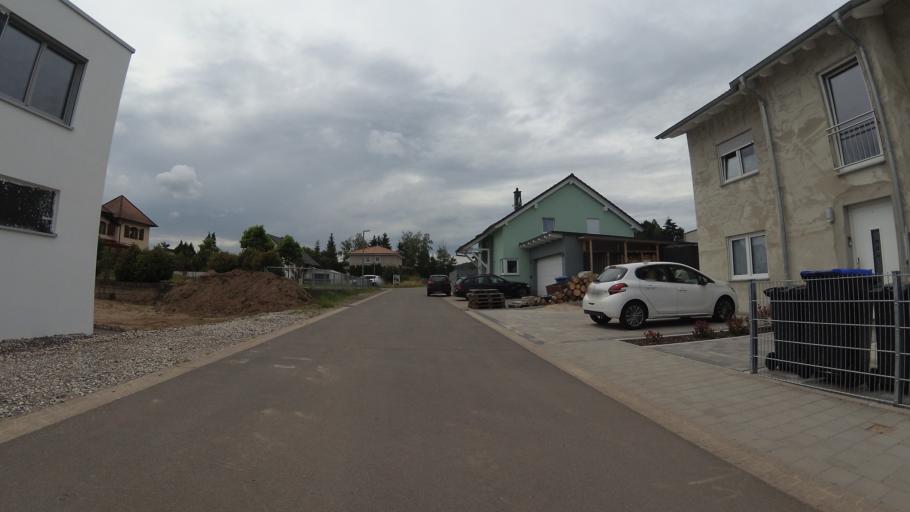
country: DE
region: Saarland
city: Wallerfangen
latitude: 49.3253
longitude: 6.7124
